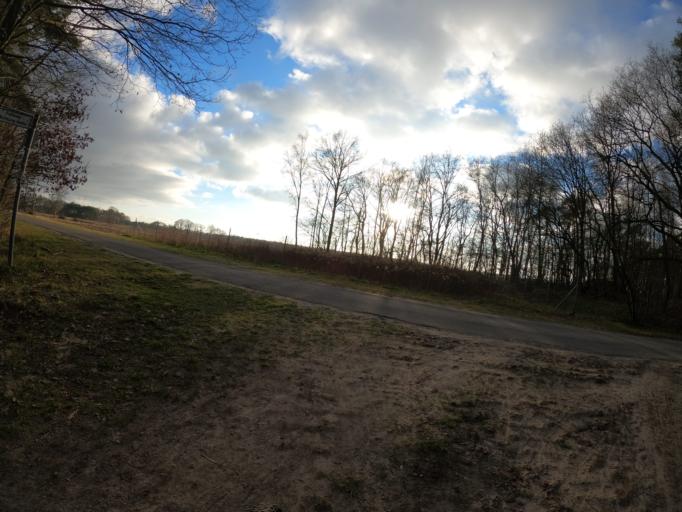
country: DE
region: Lower Saxony
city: Meppen
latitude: 52.6690
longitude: 7.3296
